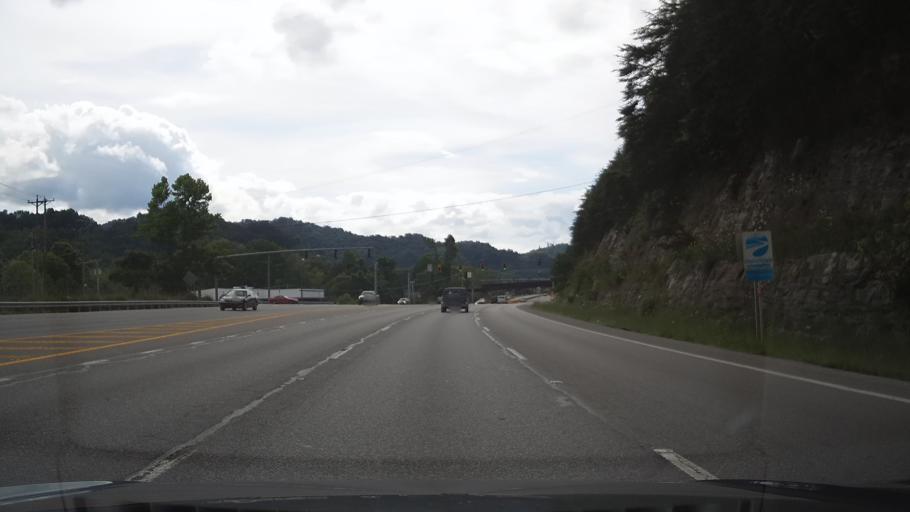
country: US
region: Kentucky
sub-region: Pike County
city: Coal Run Village
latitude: 37.5105
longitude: -82.5467
